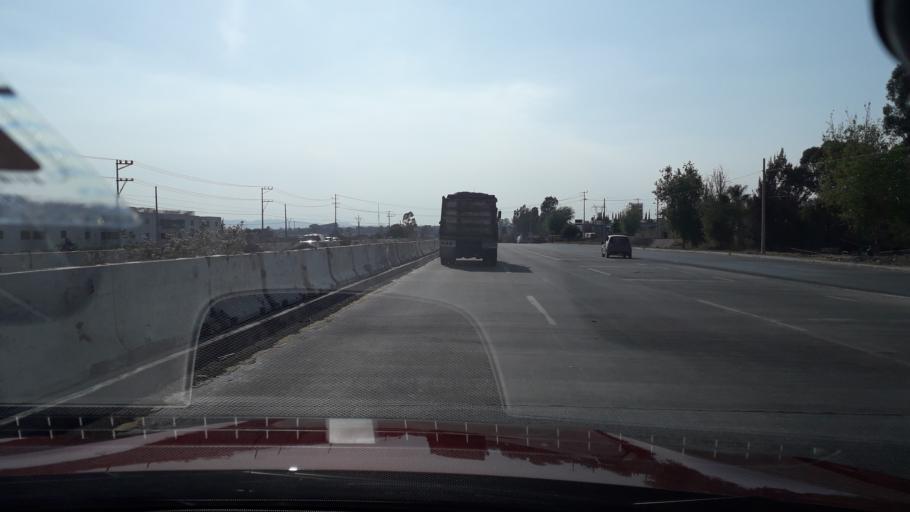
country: MX
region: Puebla
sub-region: Puebla
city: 18 de Marzo
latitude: 18.9714
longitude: -98.2013
